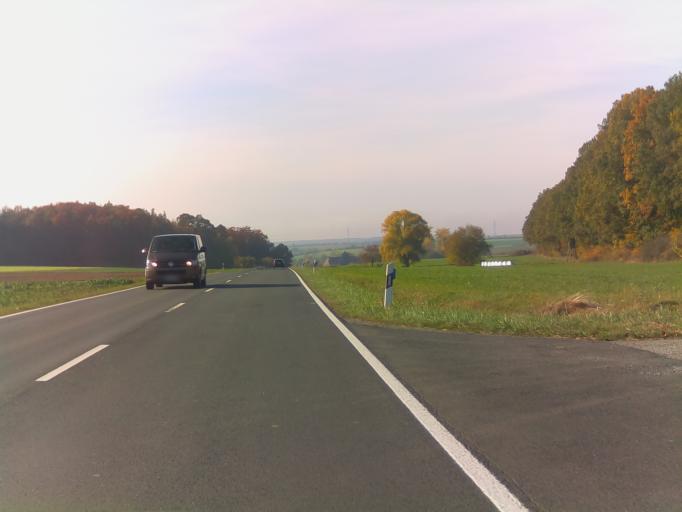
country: DE
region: Bavaria
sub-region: Regierungsbezirk Unterfranken
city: Prichsenstadt
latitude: 49.8463
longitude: 10.3720
